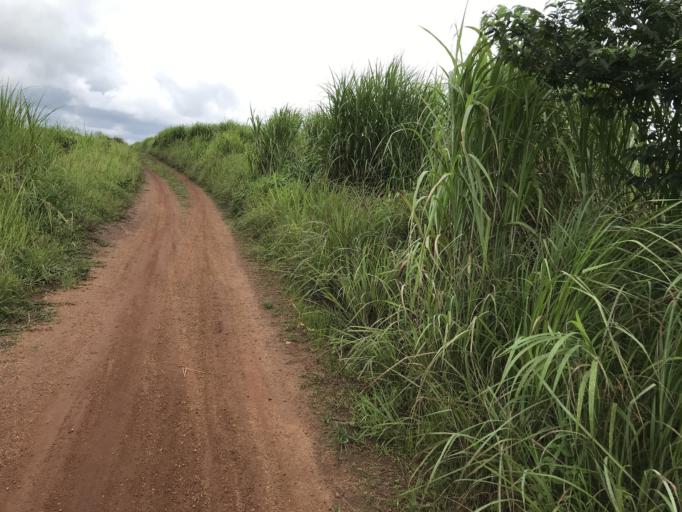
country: SL
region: Eastern Province
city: Buedu
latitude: 8.4720
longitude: -10.3175
